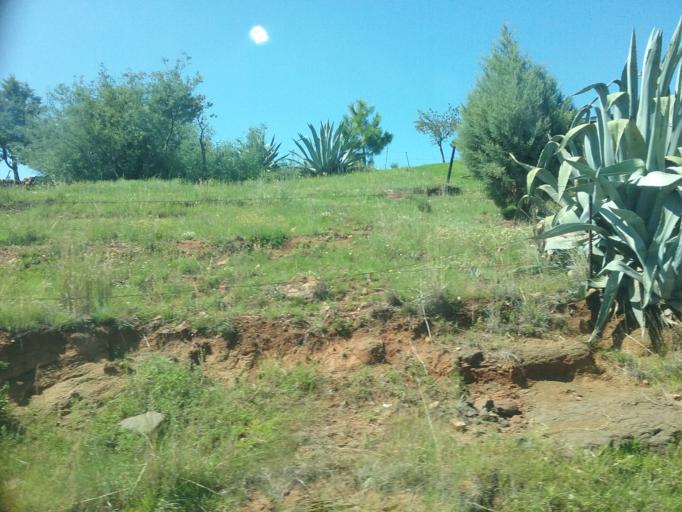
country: LS
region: Berea
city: Teyateyaneng
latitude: -29.2149
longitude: 27.8646
